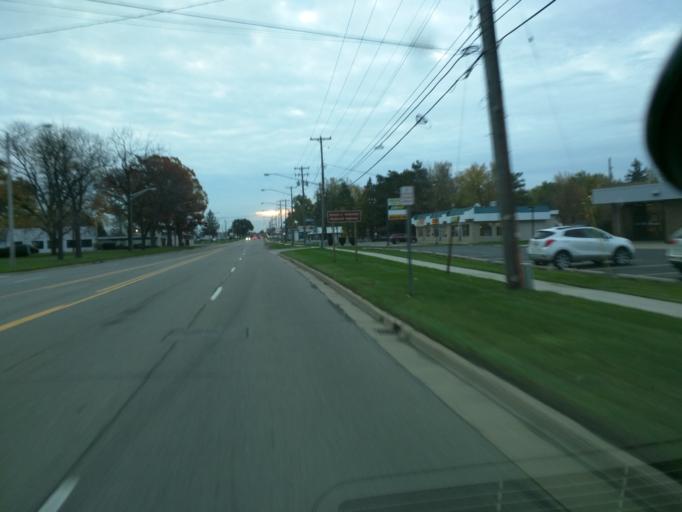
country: US
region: Michigan
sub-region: Ingham County
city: Edgemont Park
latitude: 42.7689
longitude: -84.5986
